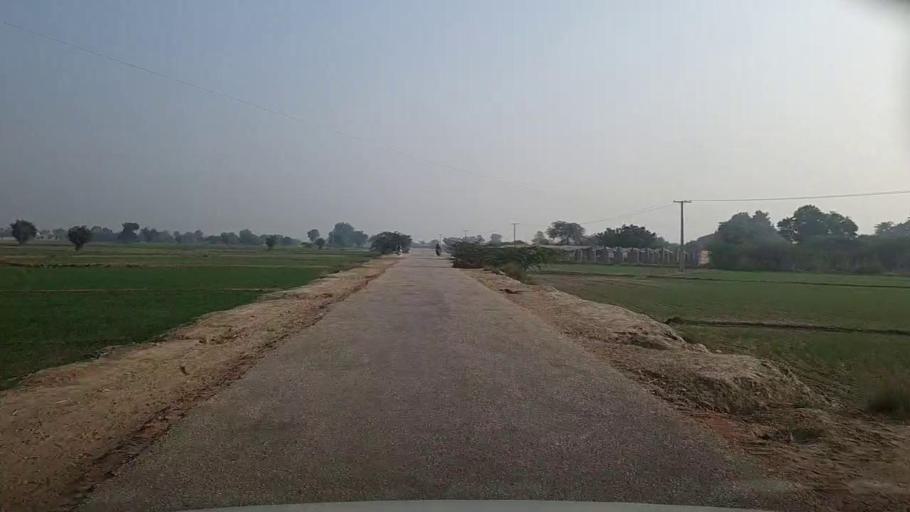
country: PK
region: Sindh
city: Kandiari
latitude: 27.0505
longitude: 68.4675
